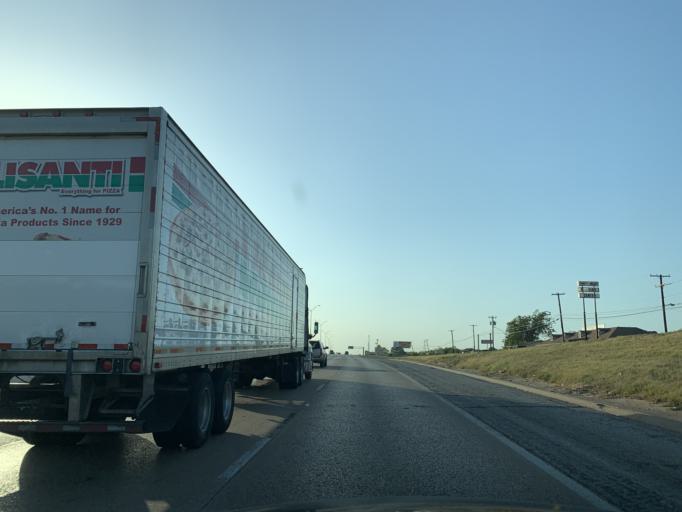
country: US
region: Texas
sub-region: Dallas County
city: Hutchins
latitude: 32.7256
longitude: -96.7017
